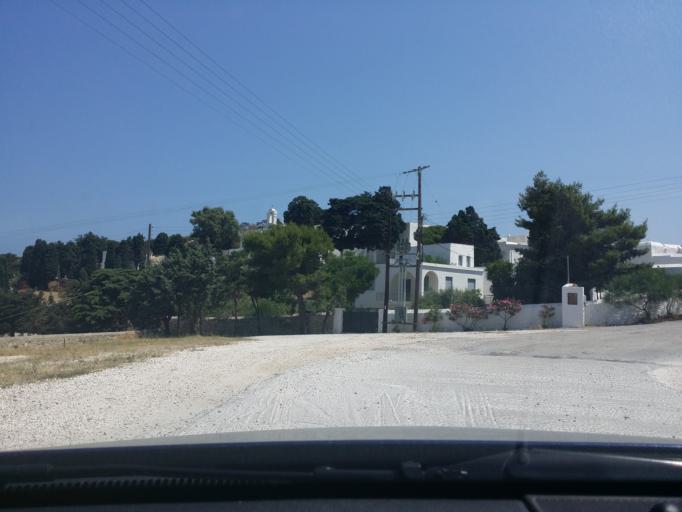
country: GR
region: South Aegean
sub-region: Nomos Kykladon
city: Paros
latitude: 37.0516
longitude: 25.1302
